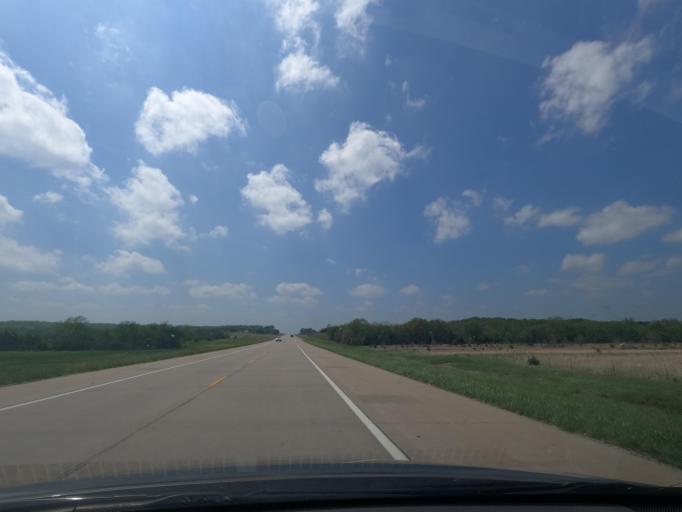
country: US
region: Kansas
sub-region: Wilson County
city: Fredonia
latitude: 37.6157
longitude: -95.9460
